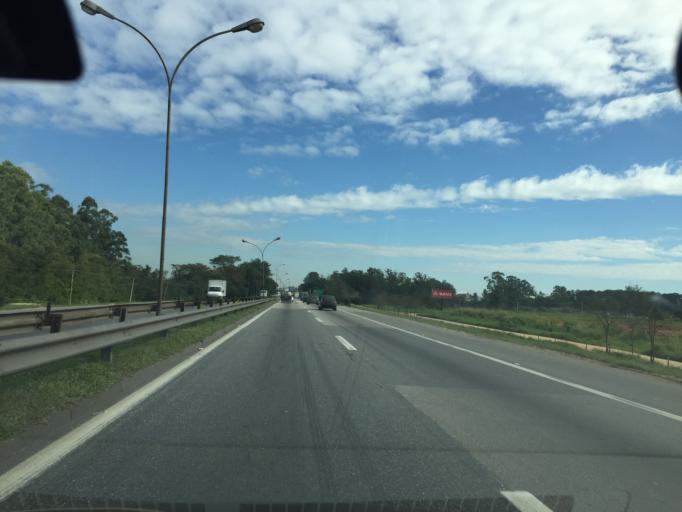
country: BR
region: Sao Paulo
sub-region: Jacarei
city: Jacarei
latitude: -23.2704
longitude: -45.9670
